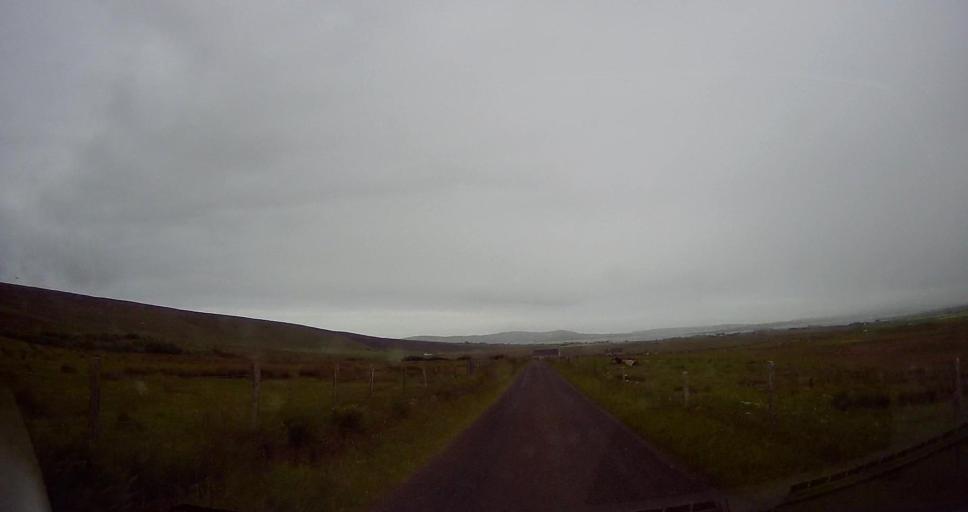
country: GB
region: Scotland
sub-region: Orkney Islands
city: Stromness
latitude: 58.9778
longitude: -3.1687
